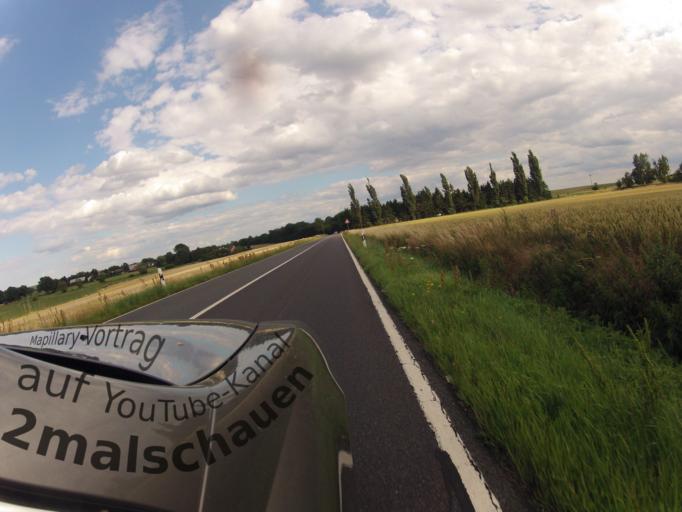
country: DE
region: Mecklenburg-Vorpommern
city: Seebad Bansin
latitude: 53.8889
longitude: 14.0815
